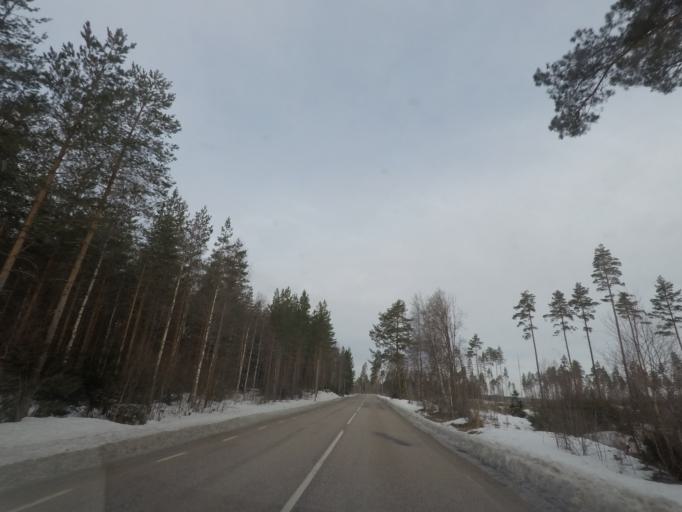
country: SE
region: Vaestmanland
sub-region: Vasteras
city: Skultuna
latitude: 59.7531
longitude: 16.3196
